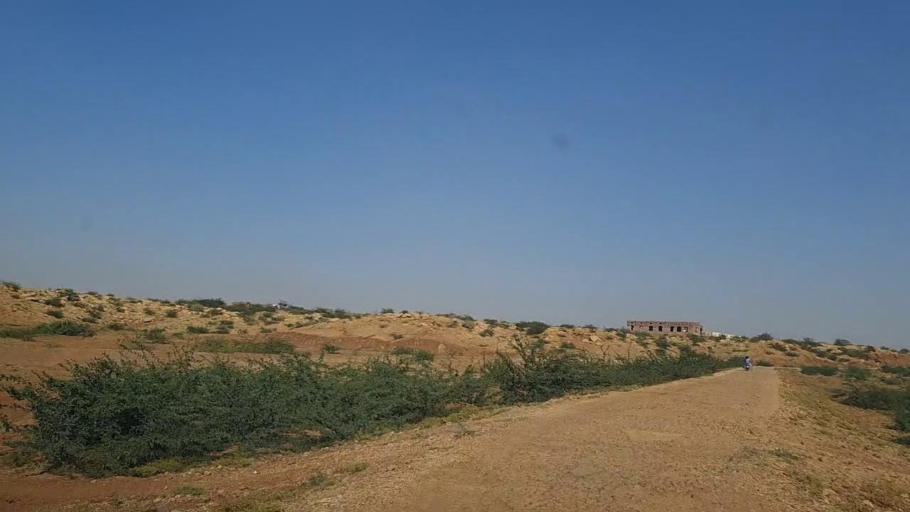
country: PK
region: Sindh
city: Daro Mehar
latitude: 24.9910
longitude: 68.1332
